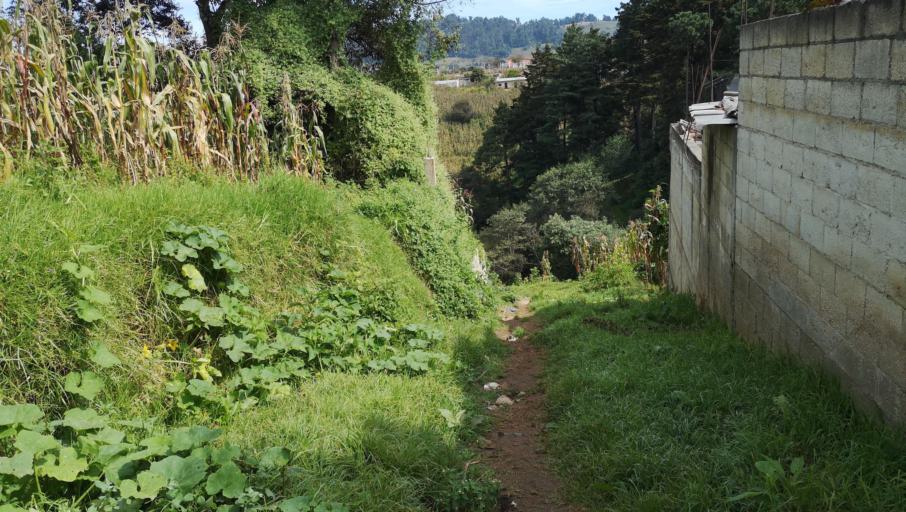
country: GT
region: Quetzaltenango
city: Cantel
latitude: 14.8193
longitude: -91.4392
